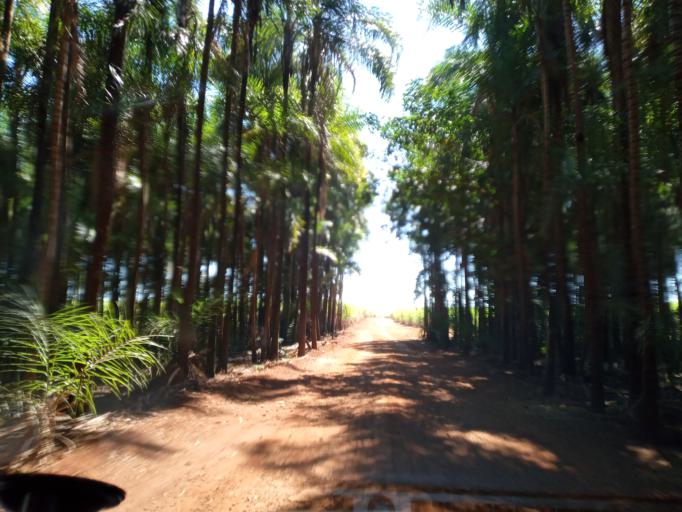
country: BR
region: Goias
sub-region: Itumbiara
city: Itumbiara
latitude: -18.4461
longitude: -49.1537
